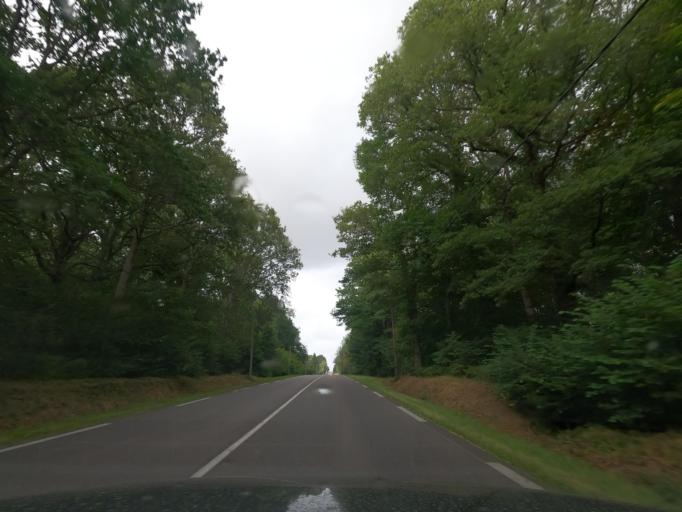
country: FR
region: Haute-Normandie
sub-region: Departement de l'Eure
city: Menneval
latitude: 49.1255
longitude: 0.6347
